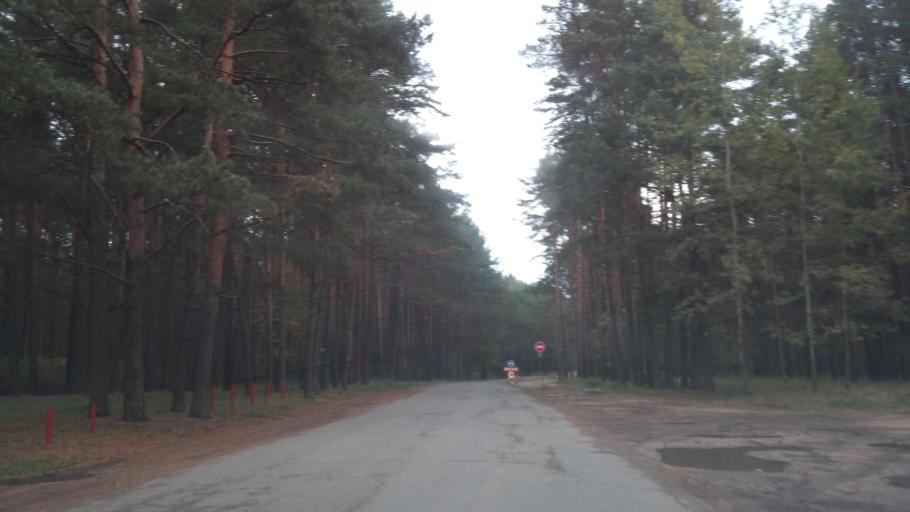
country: BY
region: Minsk
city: Zhdanovichy
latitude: 53.9515
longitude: 27.4353
